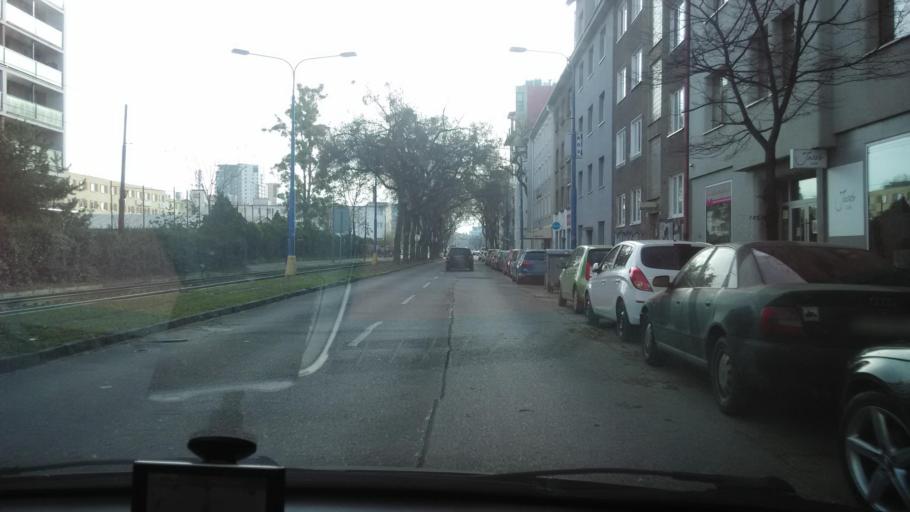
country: SK
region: Bratislavsky
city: Bratislava
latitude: 48.1567
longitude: 17.1319
